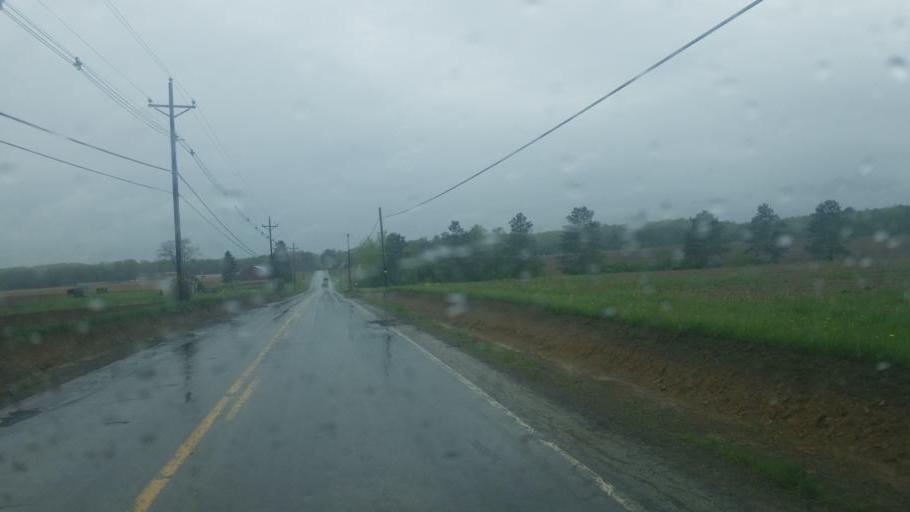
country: US
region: Pennsylvania
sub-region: Forest County
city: Tionesta
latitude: 41.3952
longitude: -79.3466
